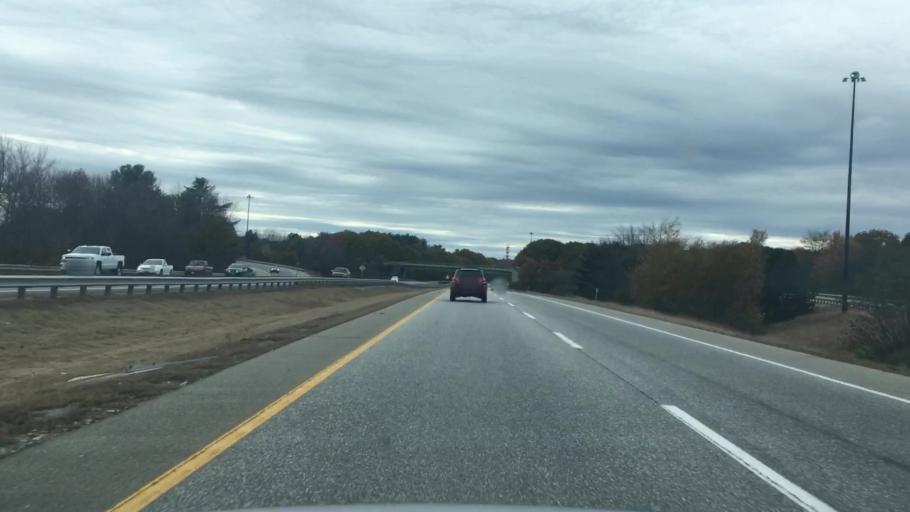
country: US
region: Maine
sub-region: Cumberland County
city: South Portland Gardens
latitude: 43.6304
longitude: -70.3146
